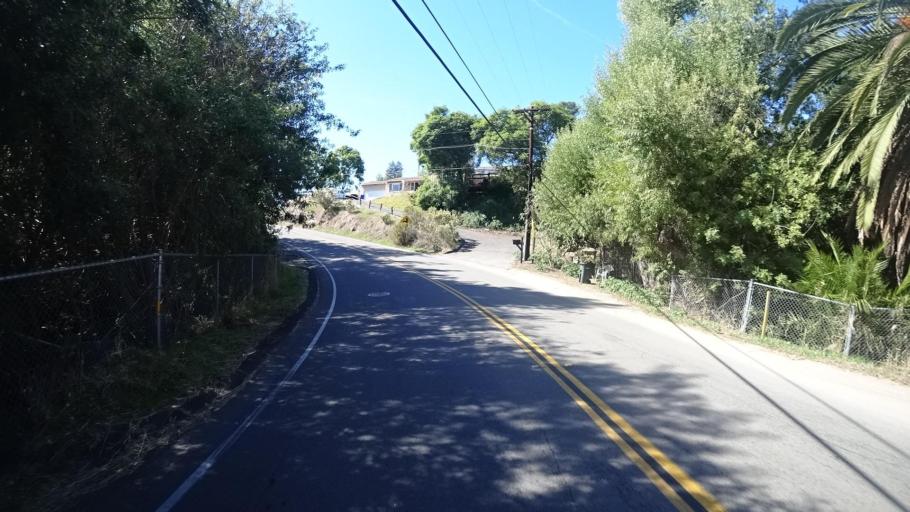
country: US
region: California
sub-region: San Diego County
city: Casa de Oro-Mount Helix
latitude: 32.7556
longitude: -116.9724
